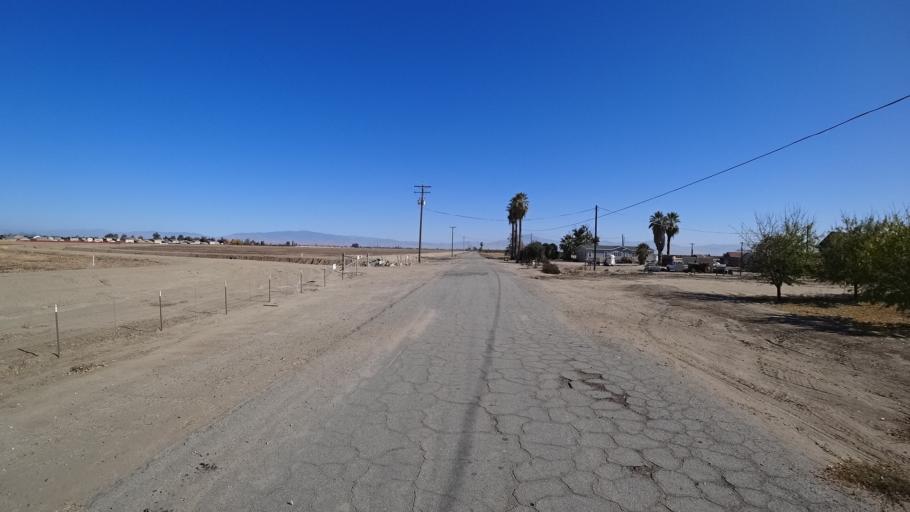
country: US
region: California
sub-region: Kern County
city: Greenfield
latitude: 35.2598
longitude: -119.0717
